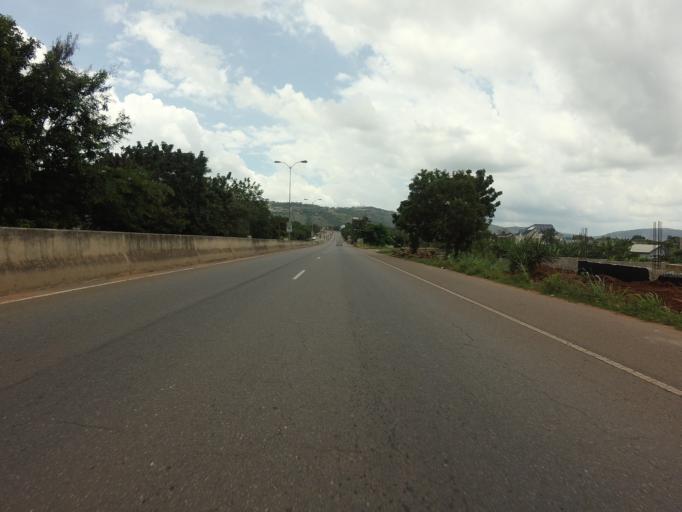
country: GH
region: Eastern
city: Aburi
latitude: 5.7769
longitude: -0.1814
